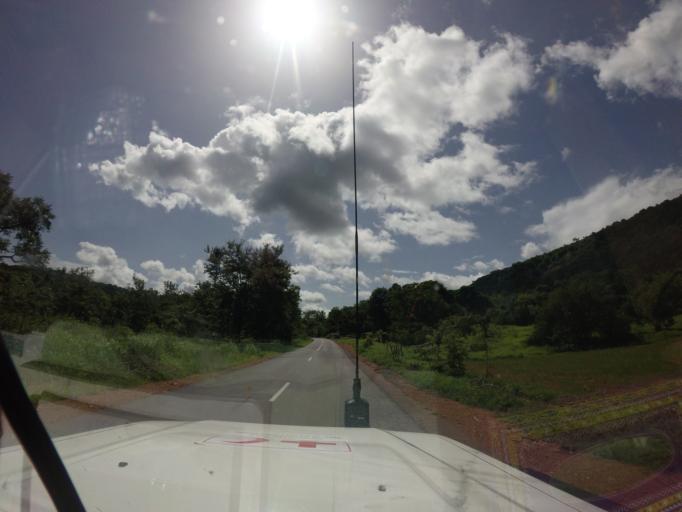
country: GN
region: Mamou
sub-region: Mamou Prefecture
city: Mamou
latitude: 10.2321
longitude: -11.8663
